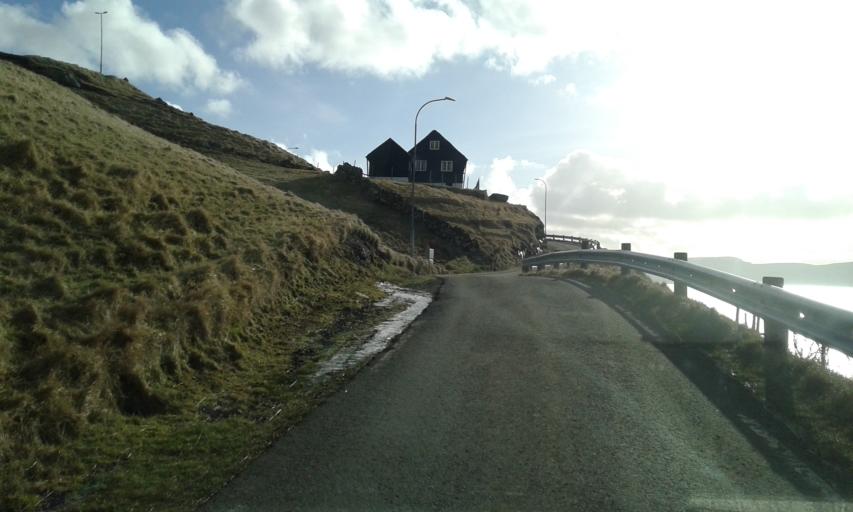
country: FO
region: Streymoy
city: Argir
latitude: 61.9847
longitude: -6.8613
